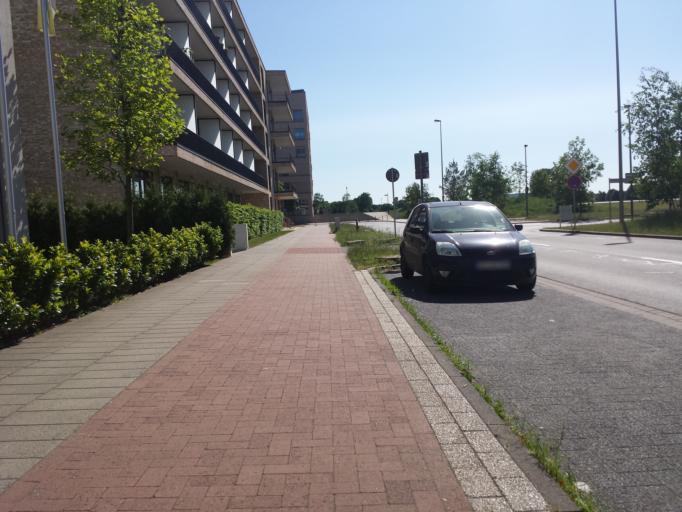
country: DE
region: Bremen
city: Bremen
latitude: 53.0989
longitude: 8.7609
